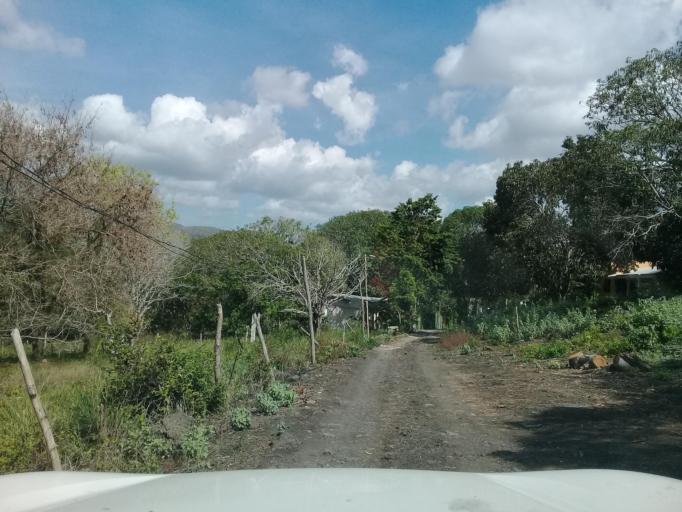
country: MX
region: Veracruz
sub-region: Emiliano Zapata
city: Plan del Rio
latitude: 19.4013
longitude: -96.6473
